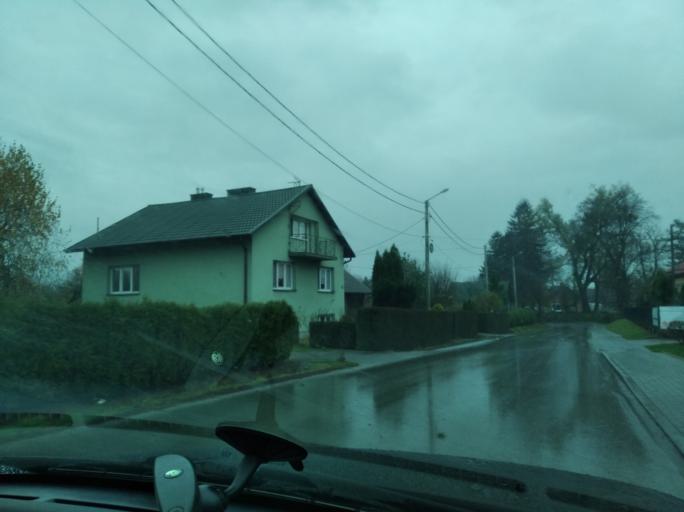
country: PL
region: Subcarpathian Voivodeship
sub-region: Powiat lancucki
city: Wysoka
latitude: 50.0438
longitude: 22.2406
